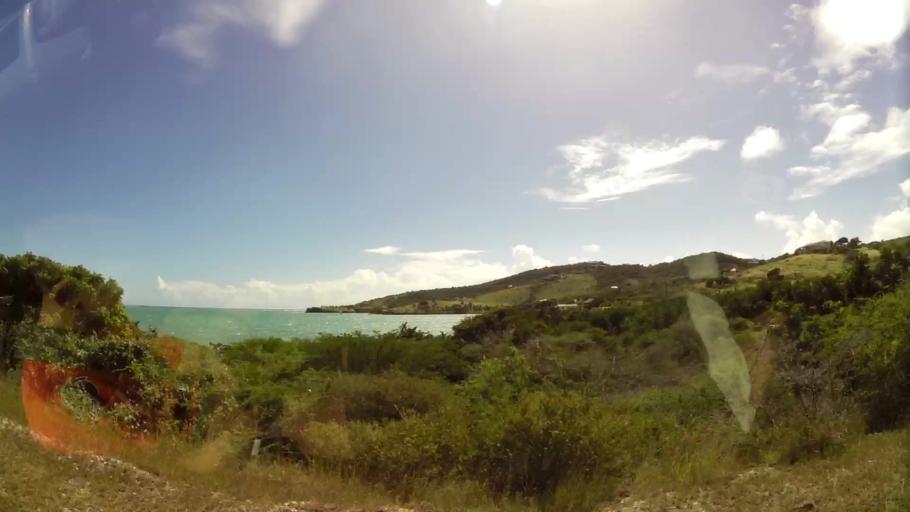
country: AG
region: Saint Paul
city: Falmouth
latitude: 17.0315
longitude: -61.7408
